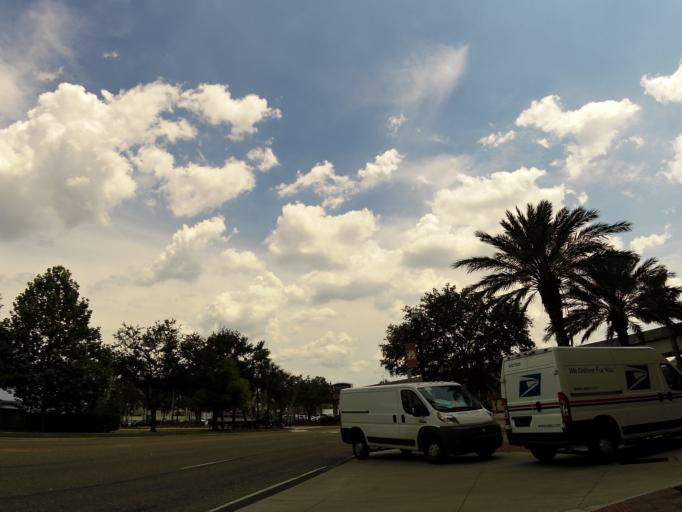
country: US
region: Florida
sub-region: Duval County
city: Jacksonville
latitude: 30.3201
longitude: -81.6527
